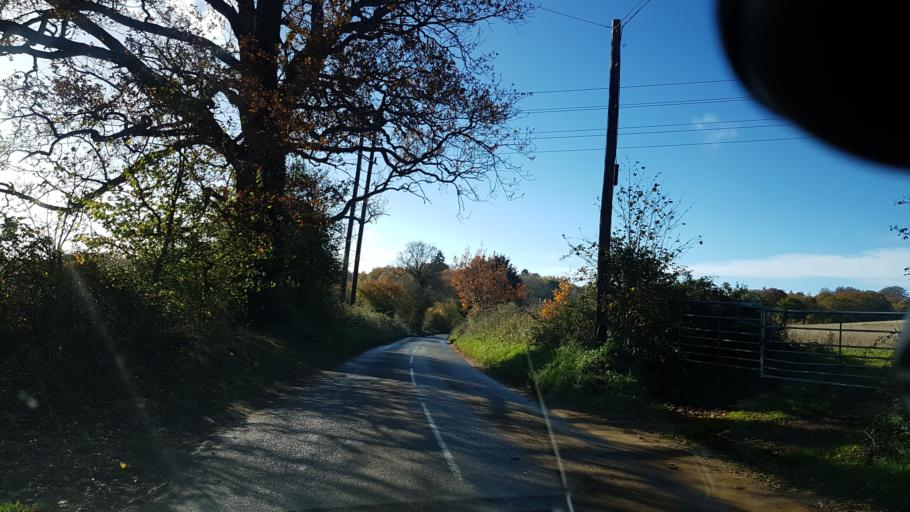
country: GB
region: England
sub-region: Surrey
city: Normandy
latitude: 51.2167
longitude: -0.6732
